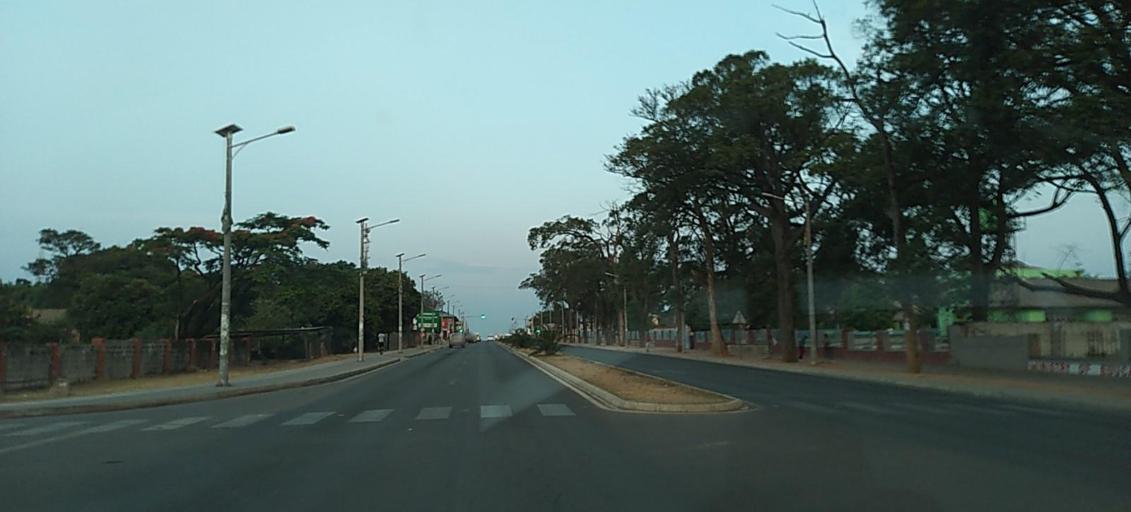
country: ZM
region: Copperbelt
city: Chingola
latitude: -12.5468
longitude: 27.8613
